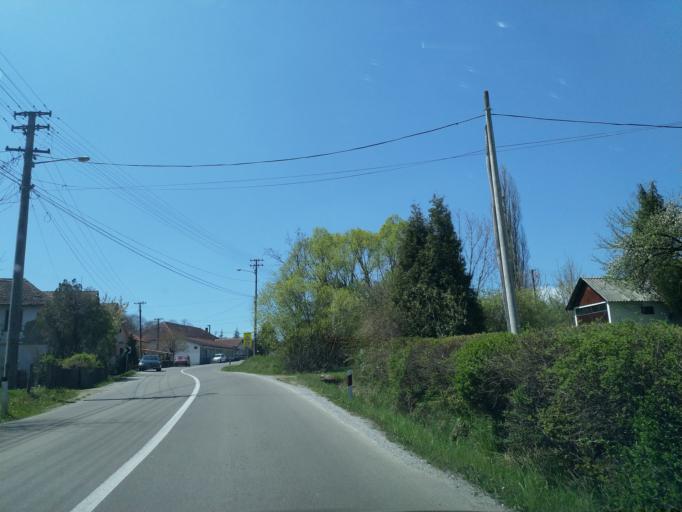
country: RS
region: Central Serbia
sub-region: Belgrade
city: Lazarevac
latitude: 44.3483
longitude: 20.3980
